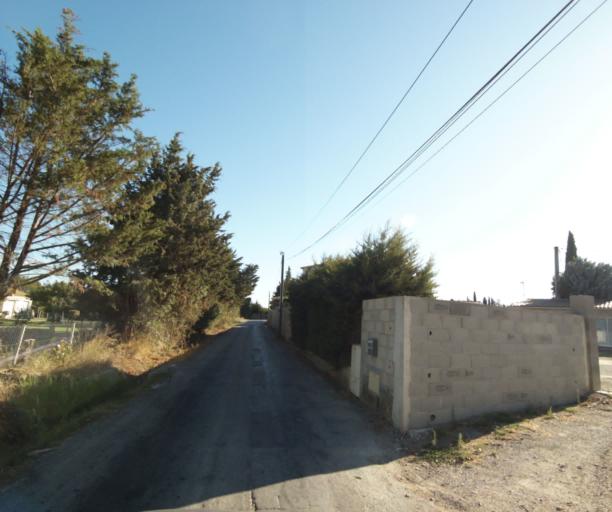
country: FR
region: Languedoc-Roussillon
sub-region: Departement du Gard
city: Bouillargues
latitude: 43.7931
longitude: 4.4378
